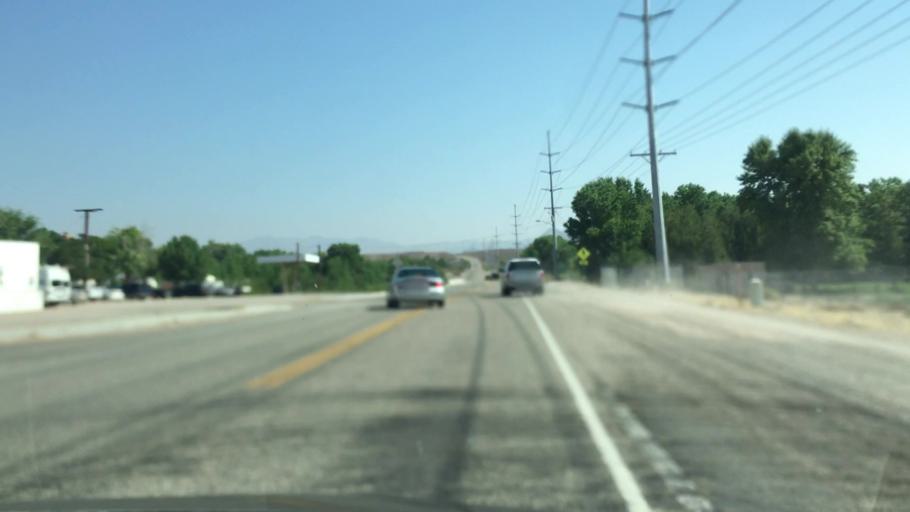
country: US
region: Arizona
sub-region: Mohave County
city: Beaver Dam
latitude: 36.8999
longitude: -113.9345
